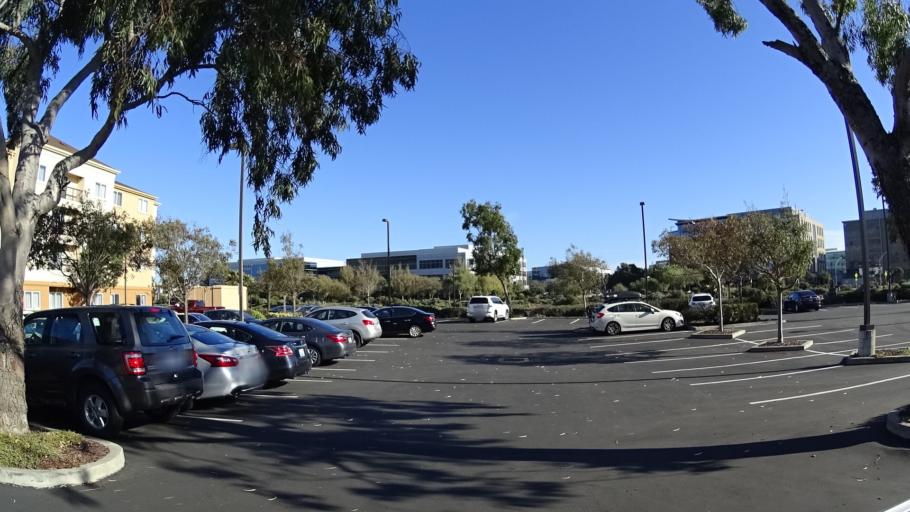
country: US
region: California
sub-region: San Mateo County
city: Brisbane
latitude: 37.6657
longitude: -122.3952
